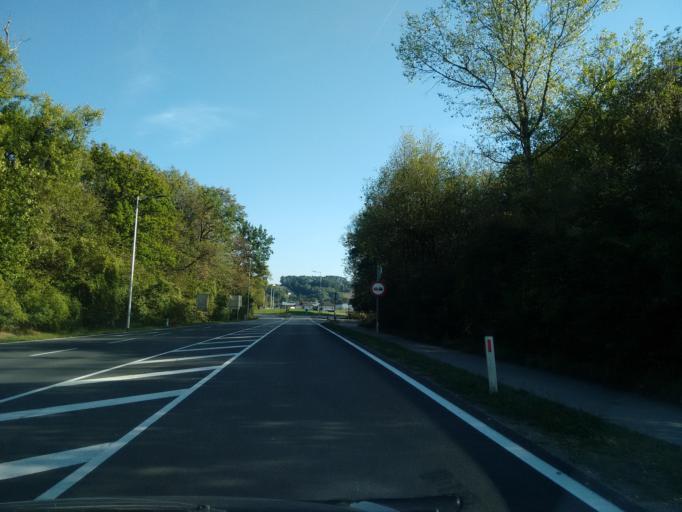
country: AT
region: Upper Austria
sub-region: Wels-Land
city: Marchtrenk
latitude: 48.1740
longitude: 14.1233
